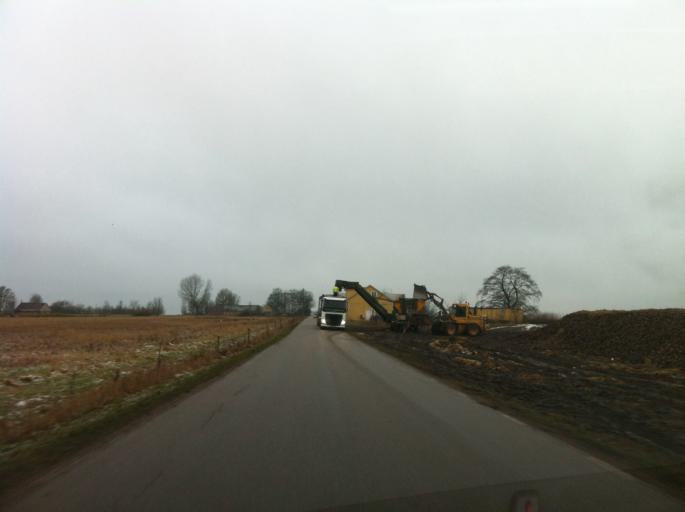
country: SE
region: Skane
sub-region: Landskrona
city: Asmundtorp
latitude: 55.9764
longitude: 12.9250
